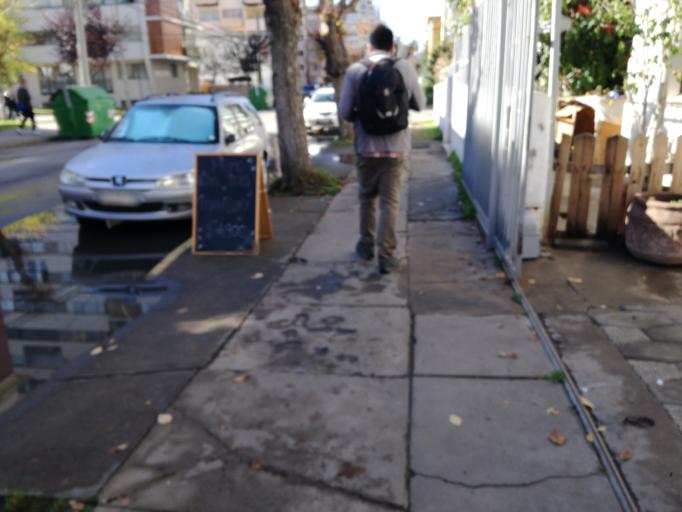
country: CL
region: Valparaiso
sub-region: Provincia de Valparaiso
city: Vina del Mar
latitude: -33.0195
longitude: -71.5577
